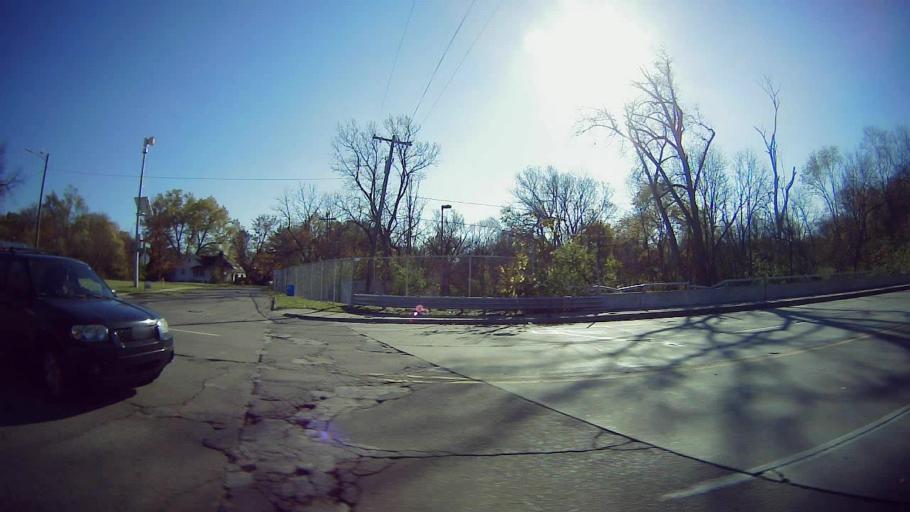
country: US
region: Michigan
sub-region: Wayne County
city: Redford
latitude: 42.4148
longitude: -83.2652
